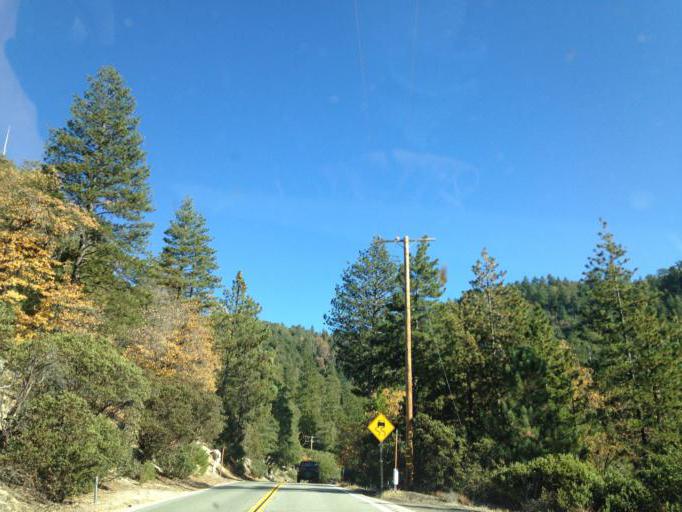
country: US
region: California
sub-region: Riverside County
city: Idyllwild-Pine Cove
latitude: 33.7775
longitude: -116.7377
